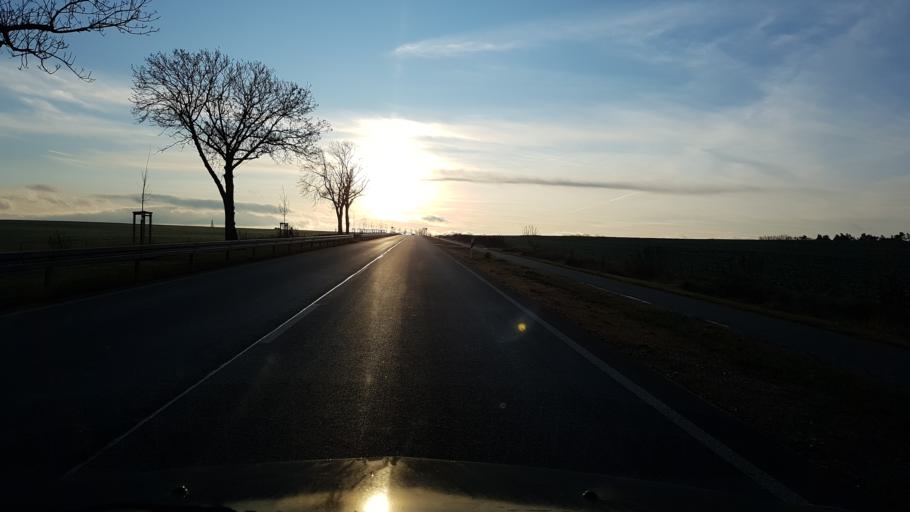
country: DE
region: Saxony
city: Radibor
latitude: 51.2332
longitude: 14.3742
